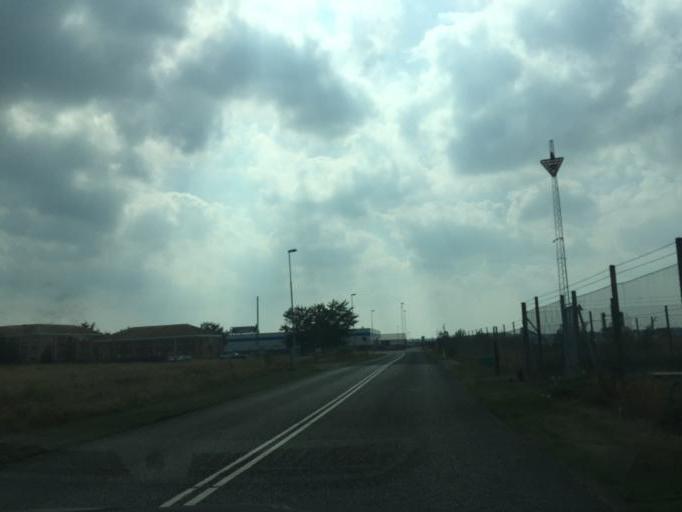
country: DK
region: South Denmark
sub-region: Nyborg Kommune
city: Nyborg
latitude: 55.2997
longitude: 10.8170
